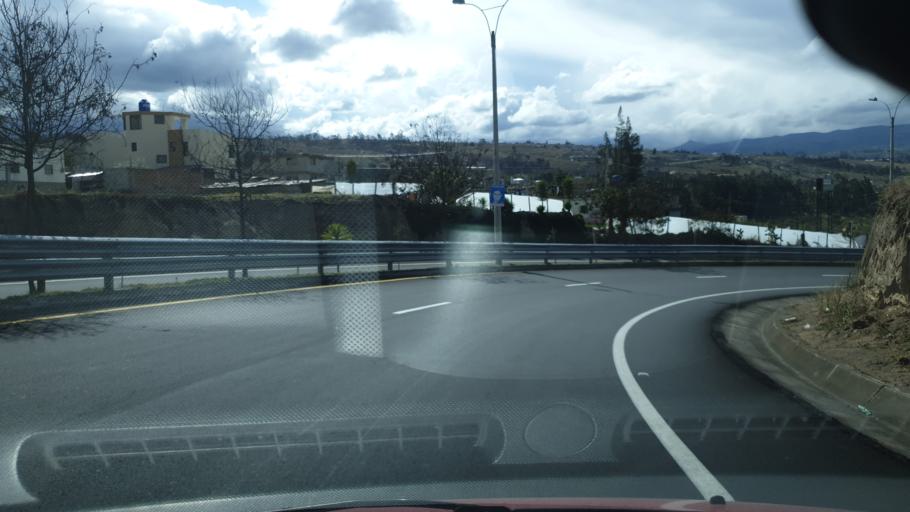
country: EC
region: Tungurahua
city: Ambato
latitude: -1.3038
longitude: -78.6380
